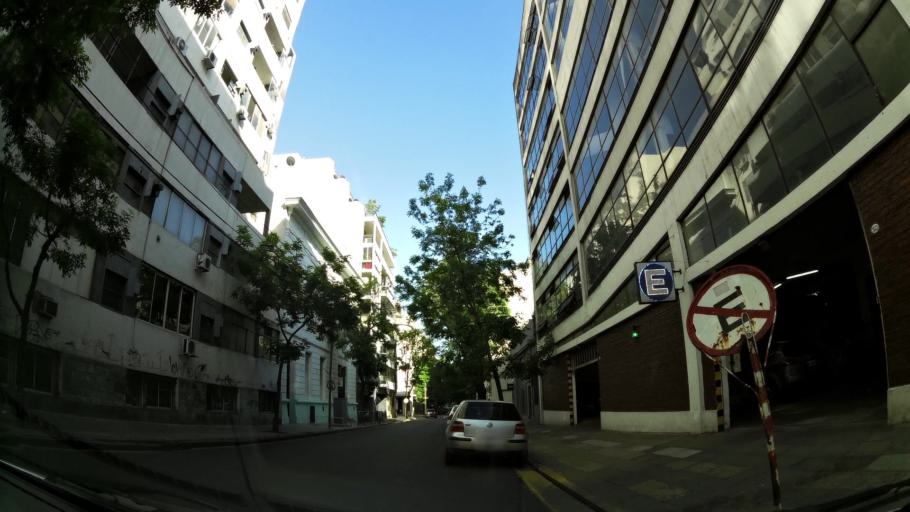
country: AR
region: Buenos Aires F.D.
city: Retiro
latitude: -34.5882
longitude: -58.4013
